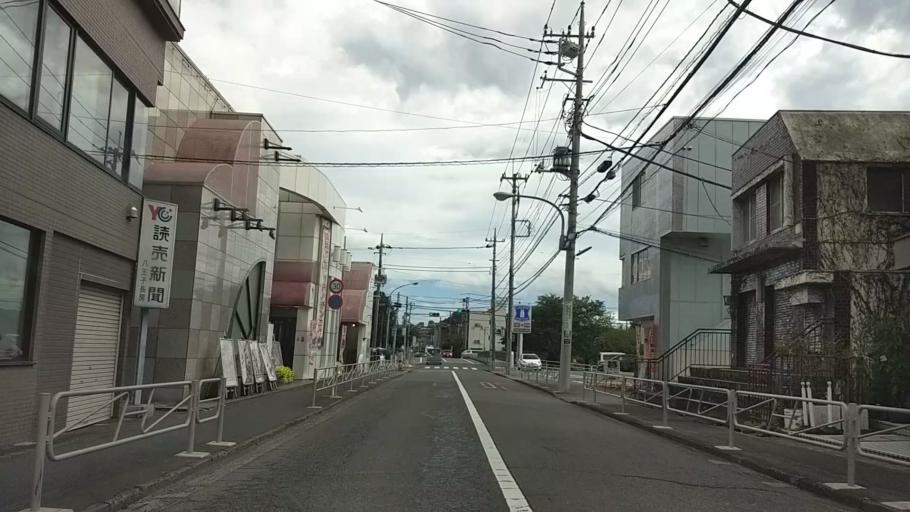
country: JP
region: Tokyo
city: Hachioji
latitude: 35.6542
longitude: 139.2994
